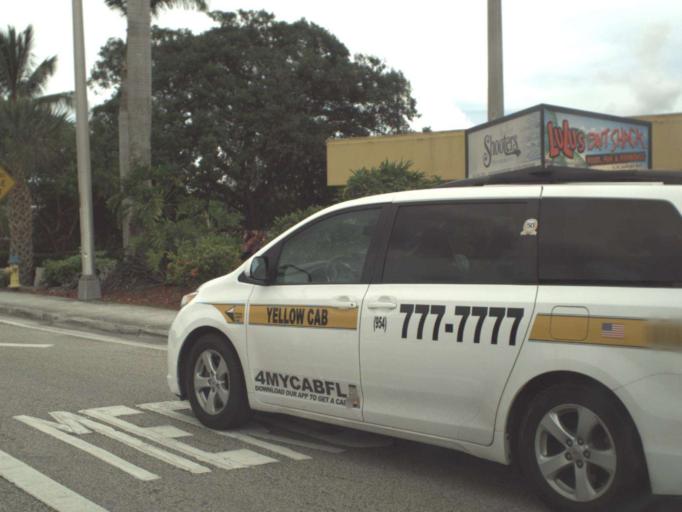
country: US
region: Florida
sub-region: Miami-Dade County
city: North Miami Beach
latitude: 25.9264
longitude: -80.1535
